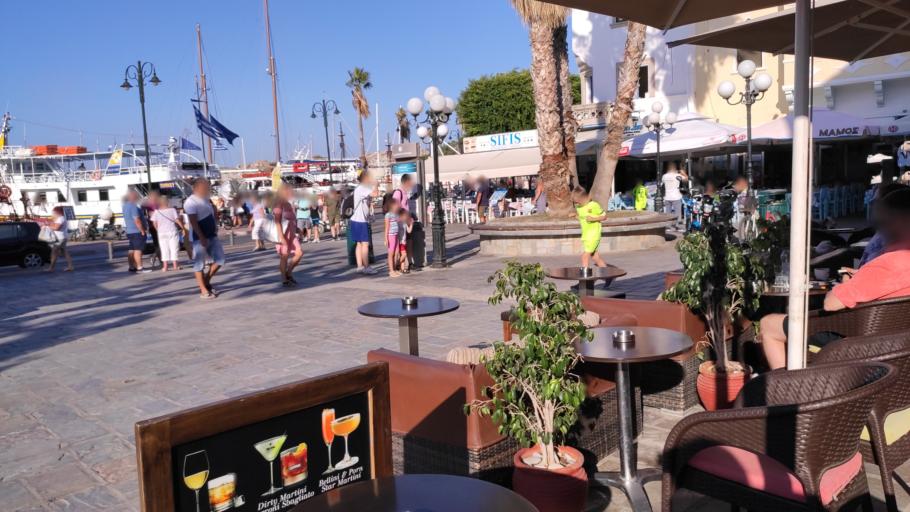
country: GR
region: South Aegean
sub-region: Nomos Dodekanisou
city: Kos
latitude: 36.8943
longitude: 27.2874
